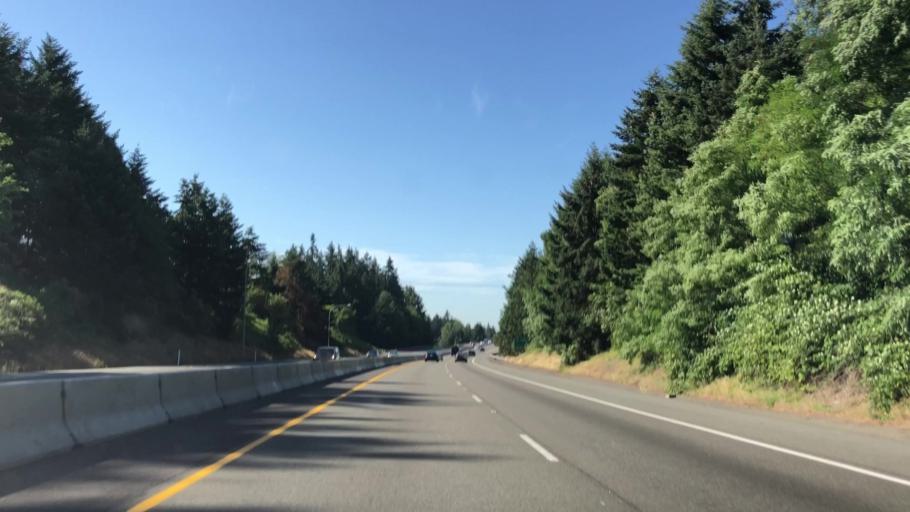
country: US
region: Washington
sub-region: King County
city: Boulevard Park
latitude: 47.4939
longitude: -122.3252
